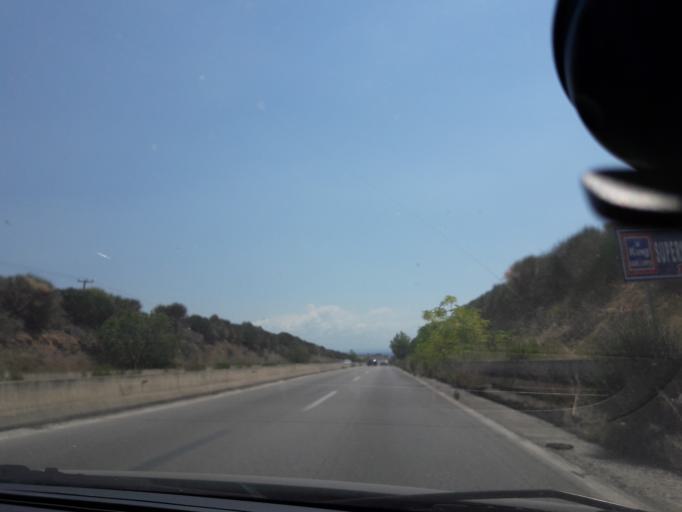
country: GR
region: Central Macedonia
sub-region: Nomos Chalkidikis
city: Nea Triglia
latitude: 40.2958
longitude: 23.1396
